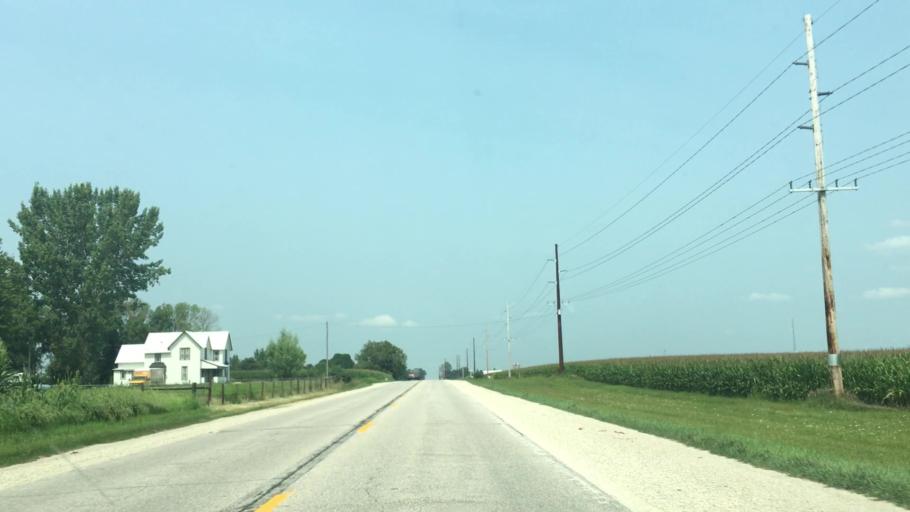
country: US
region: Iowa
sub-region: Buchanan County
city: Independence
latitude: 42.4304
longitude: -91.8897
